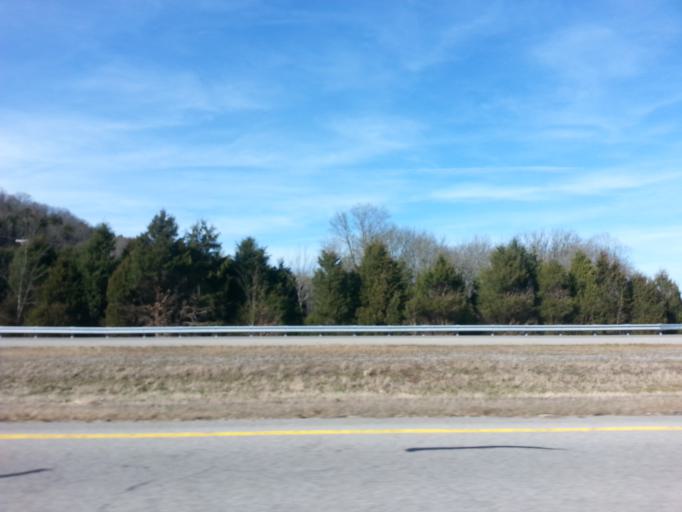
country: US
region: Tennessee
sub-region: Cannon County
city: Woodbury
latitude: 35.8091
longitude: -86.2011
